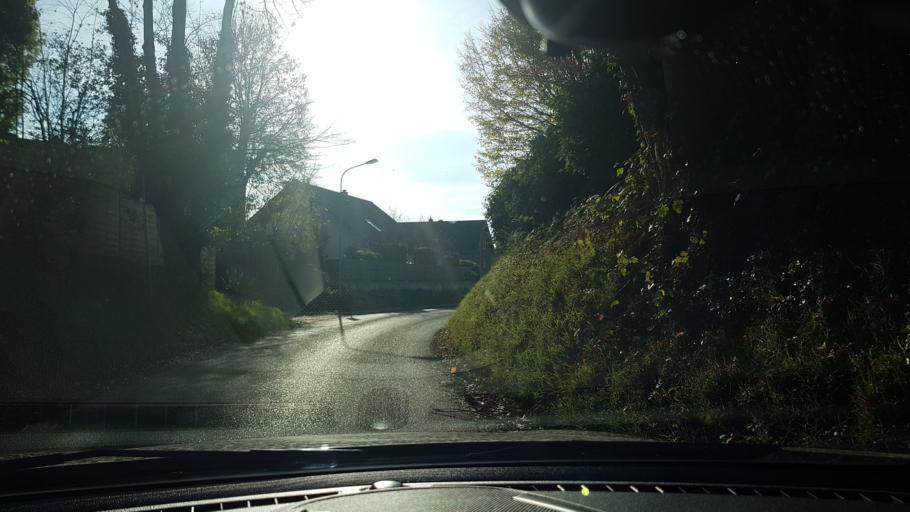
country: DE
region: North Rhine-Westphalia
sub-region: Regierungsbezirk Dusseldorf
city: Grevenbroich
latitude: 51.1253
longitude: 6.5887
